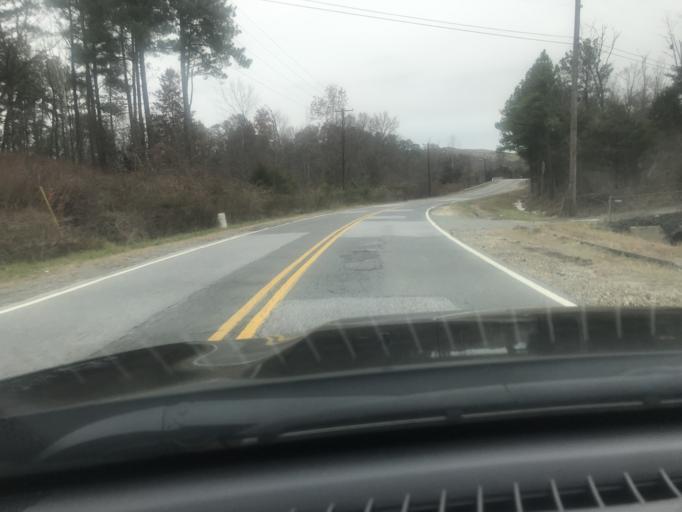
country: US
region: Maryland
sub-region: Prince George's County
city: Oxon Hill
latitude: 38.7900
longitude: -76.9774
